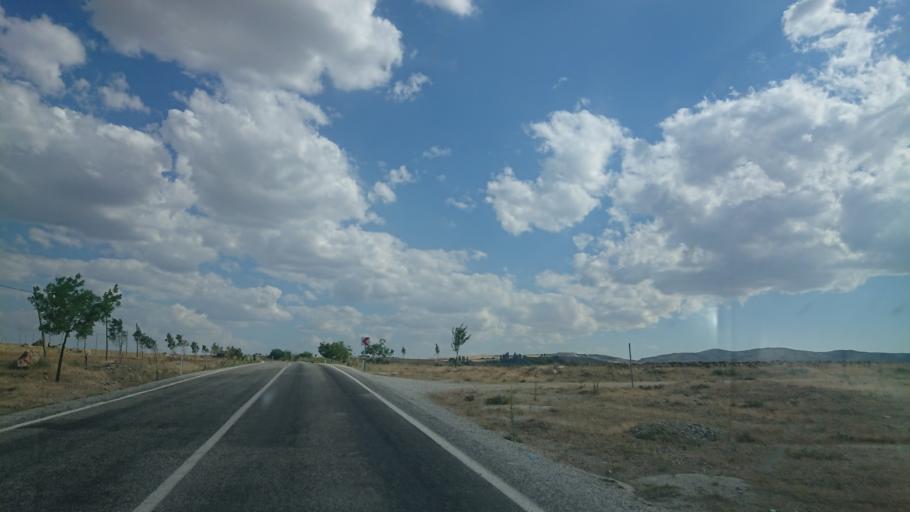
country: TR
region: Aksaray
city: Sariyahsi
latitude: 38.9585
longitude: 33.8376
